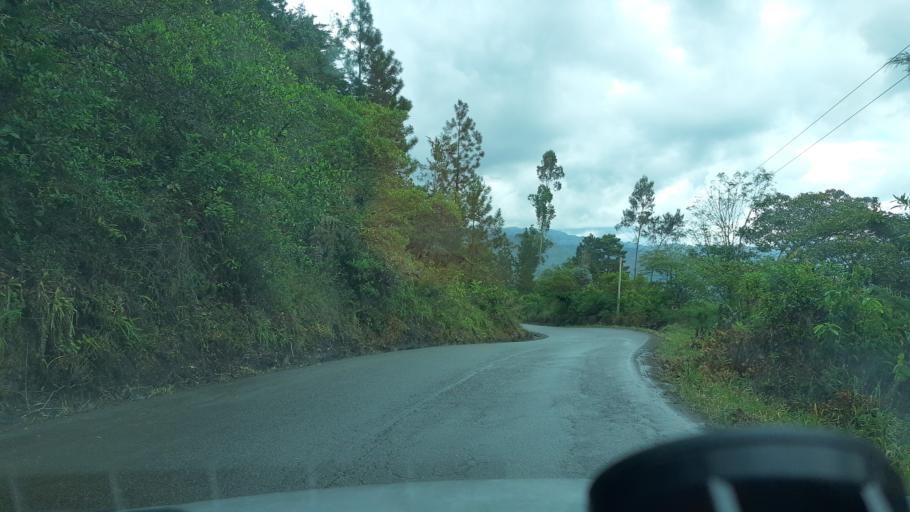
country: CO
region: Boyaca
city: Chinavita
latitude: 5.1549
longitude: -73.3696
